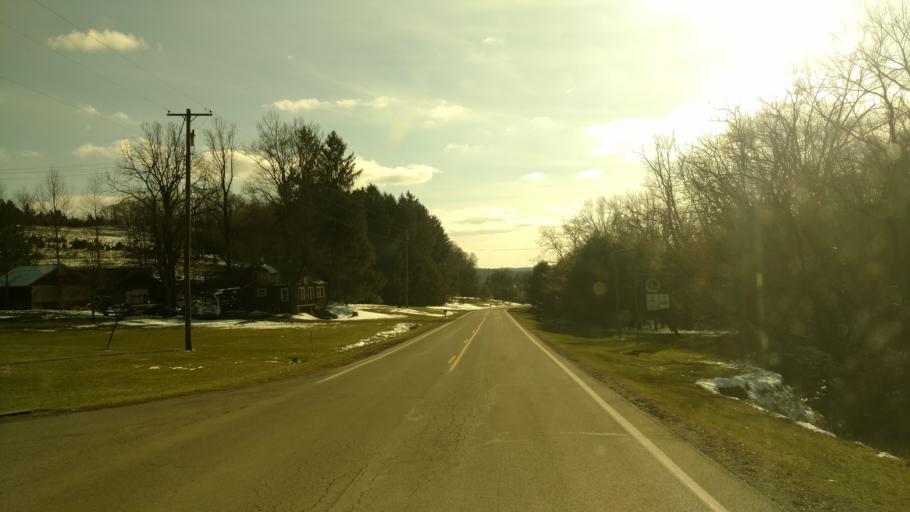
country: US
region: Ohio
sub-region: Ashland County
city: Loudonville
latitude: 40.6682
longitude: -82.3050
